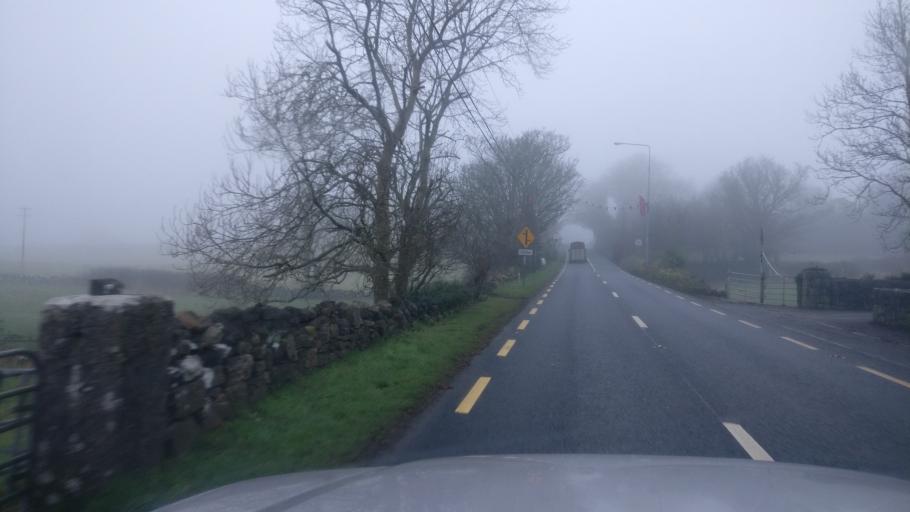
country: IE
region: Connaught
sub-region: County Galway
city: Loughrea
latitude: 53.1770
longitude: -8.6555
